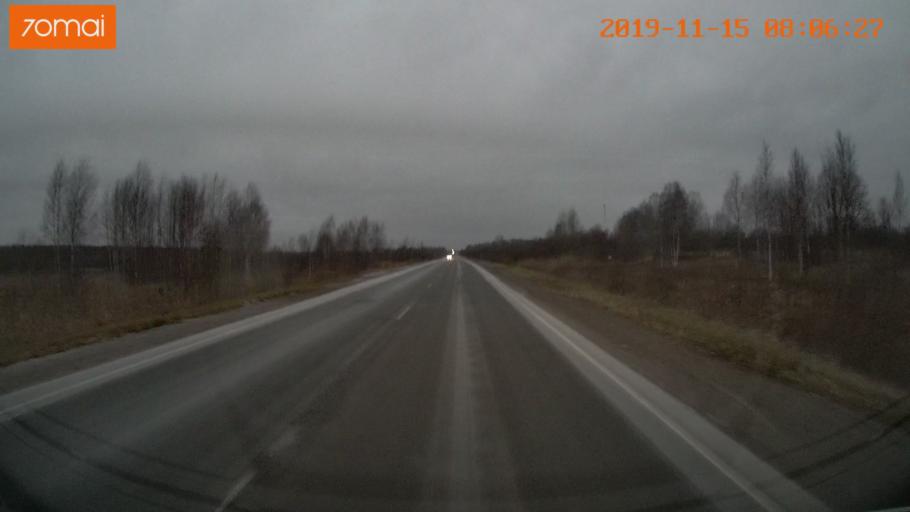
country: RU
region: Vologda
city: Cherepovets
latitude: 59.0224
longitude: 38.0376
